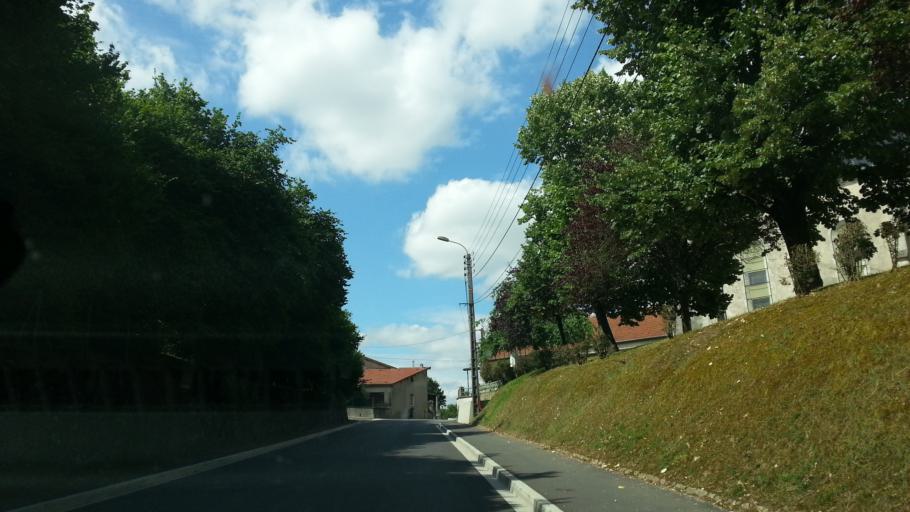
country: FR
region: Lorraine
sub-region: Departement de la Meuse
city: Thierville-sur-Meuse
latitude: 49.1601
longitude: 5.3636
